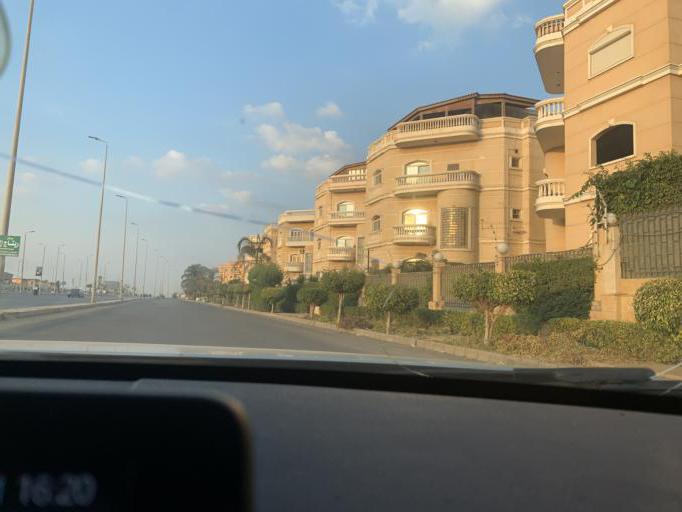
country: EG
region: Muhafazat al Qalyubiyah
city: Al Khankah
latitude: 30.0144
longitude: 31.4751
